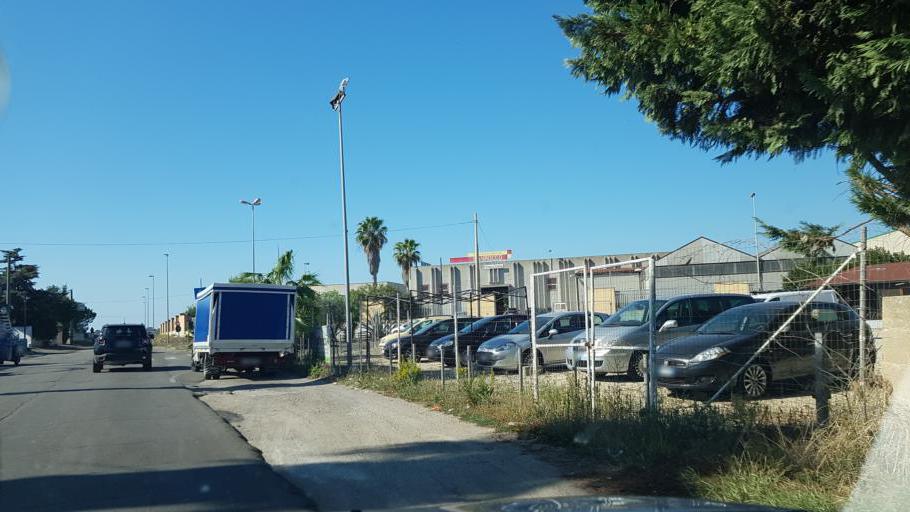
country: IT
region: Apulia
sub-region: Provincia di Lecce
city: Leverano
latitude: 40.2951
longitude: 17.9890
